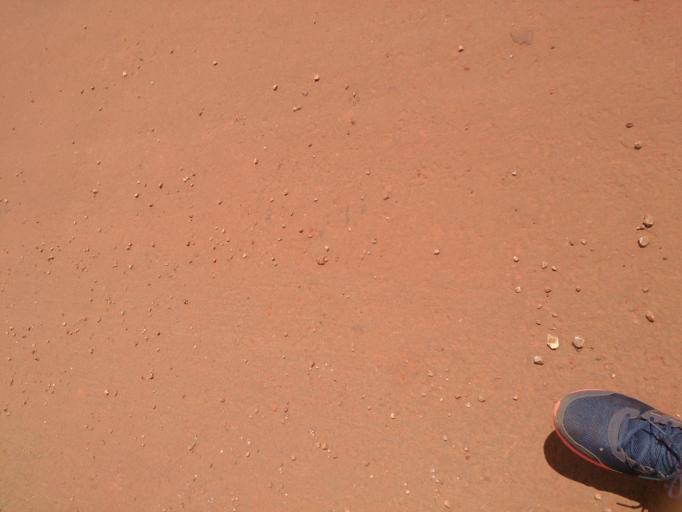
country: AR
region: Misiones
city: Campo Viera
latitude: -27.3671
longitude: -55.0475
